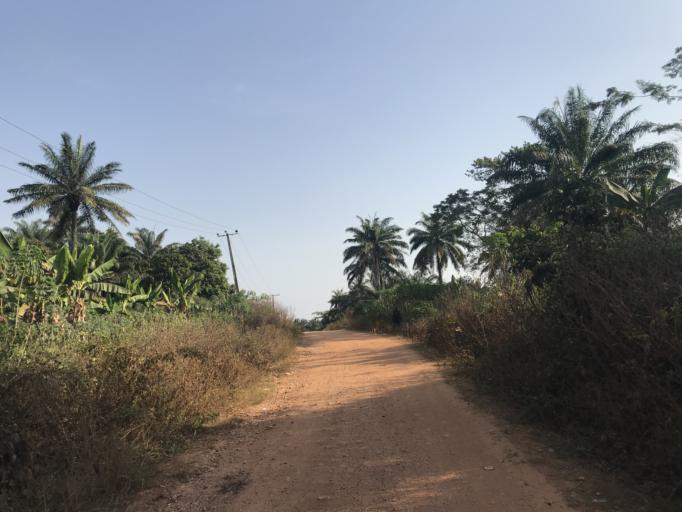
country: NG
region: Osun
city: Awo
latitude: 7.7622
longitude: 4.3138
